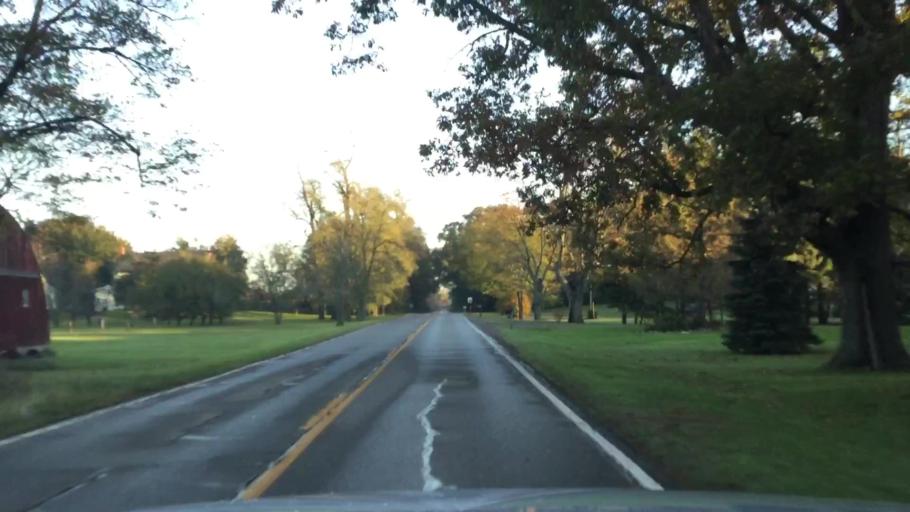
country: US
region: Michigan
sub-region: Genesee County
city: Argentine
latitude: 42.7311
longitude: -83.9490
